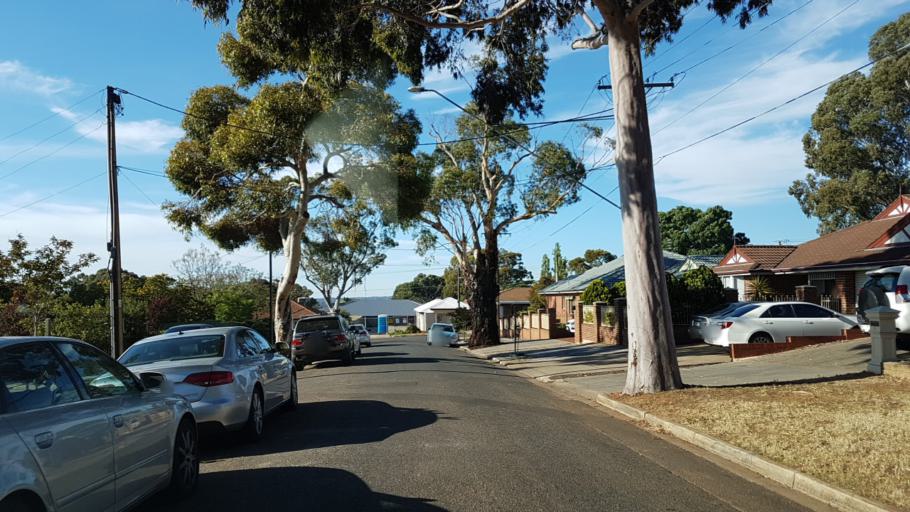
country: AU
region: South Australia
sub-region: Campbelltown
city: Campbelltown
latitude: -34.9013
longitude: 138.6814
